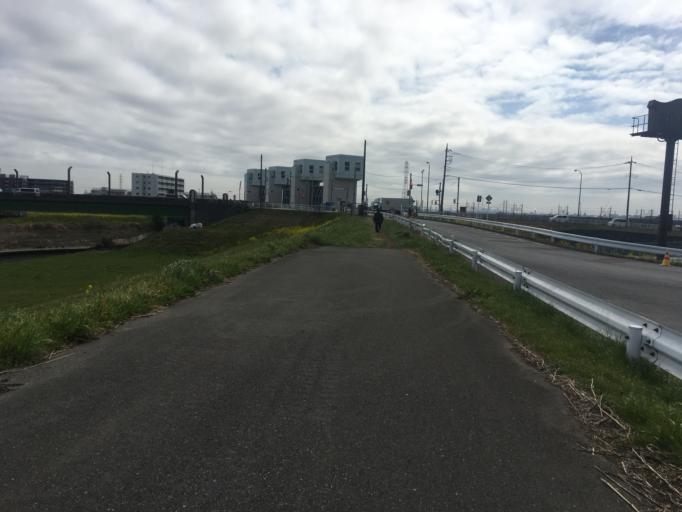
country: JP
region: Saitama
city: Shiki
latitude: 35.8416
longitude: 139.6172
